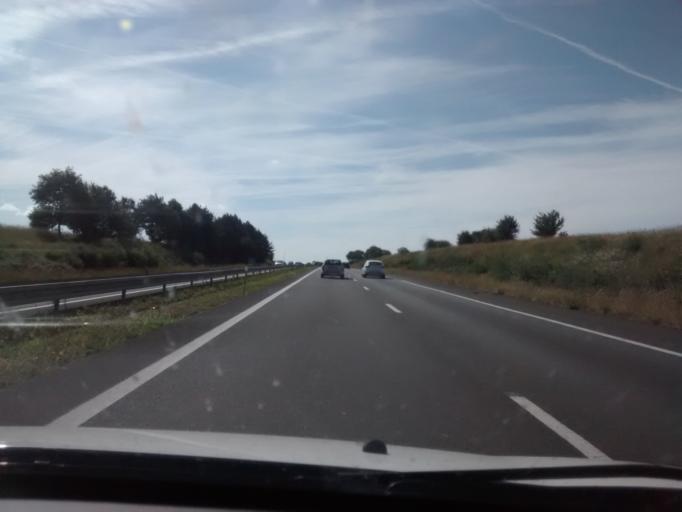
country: FR
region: Pays de la Loire
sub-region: Departement de la Mayenne
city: Soulge-sur-Ouette
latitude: 48.0656
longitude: -0.5391
